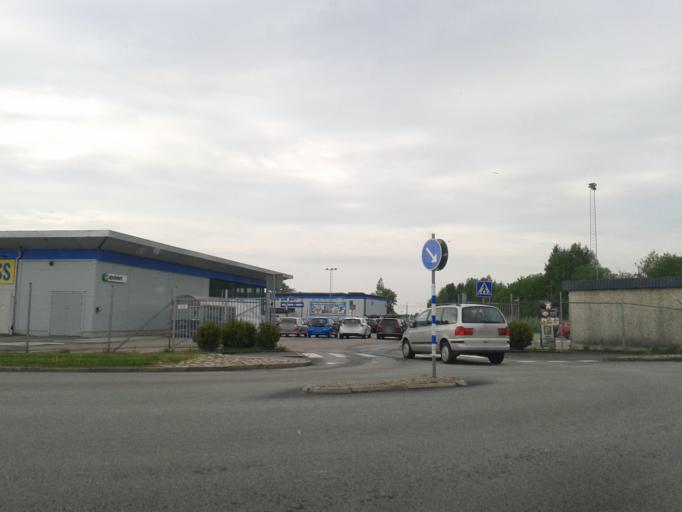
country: SE
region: Vaestra Goetaland
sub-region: Kungalvs Kommun
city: Kungalv
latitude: 57.8599
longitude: 11.9173
